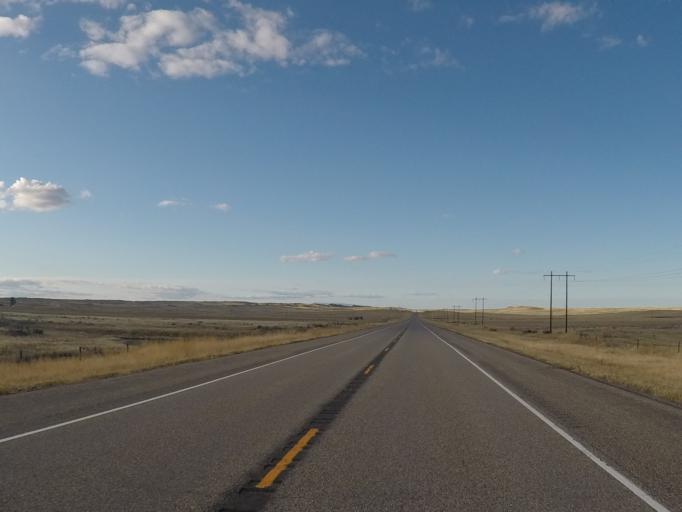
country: US
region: Montana
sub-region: Golden Valley County
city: Ryegate
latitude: 46.1996
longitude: -108.9184
